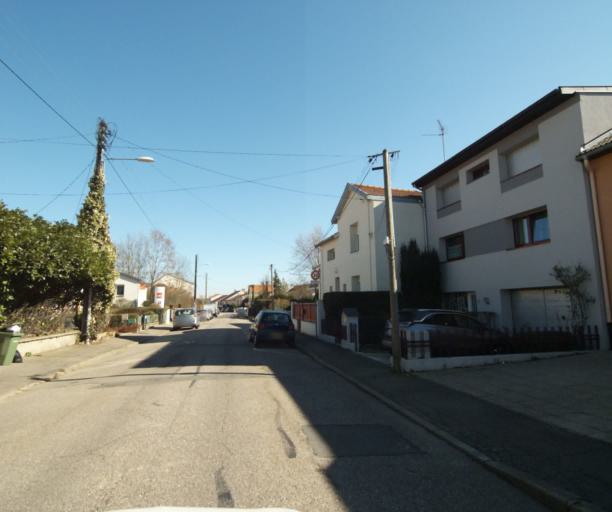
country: FR
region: Lorraine
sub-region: Departement de Meurthe-et-Moselle
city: Essey-les-Nancy
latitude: 48.7067
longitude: 6.2288
